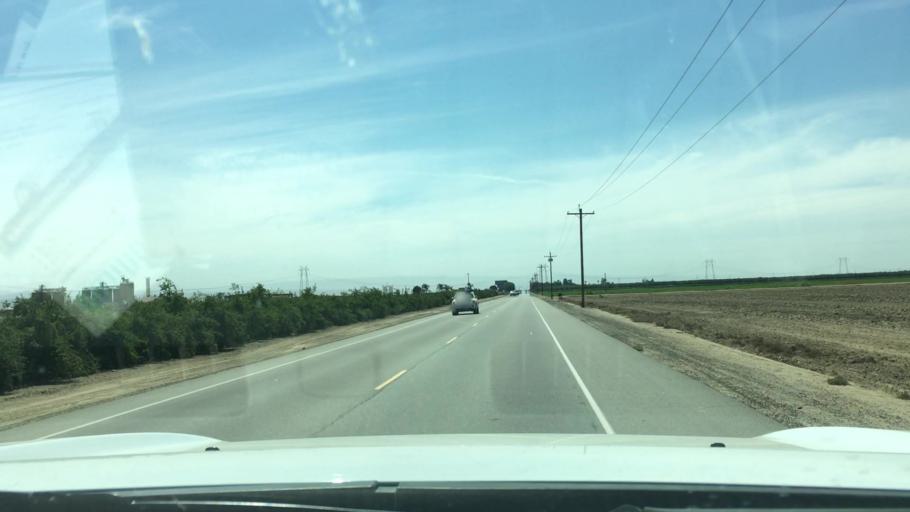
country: US
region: California
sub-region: Kern County
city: Rosedale
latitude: 35.3543
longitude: -119.2231
